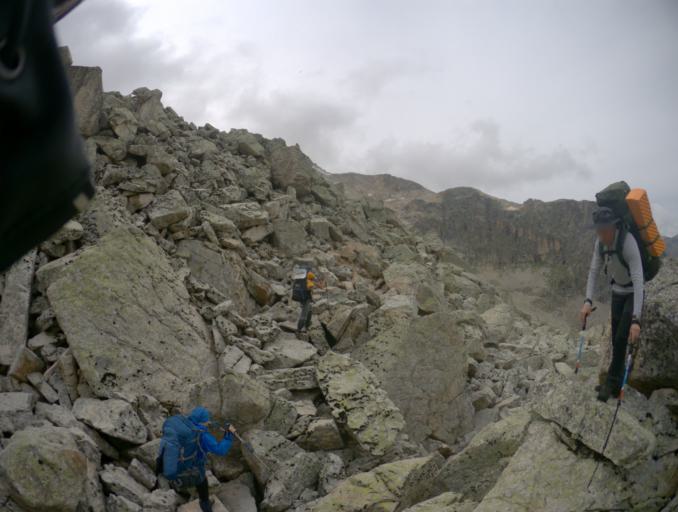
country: RU
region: Karachayevo-Cherkesiya
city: Uchkulan
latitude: 43.2855
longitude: 42.1015
